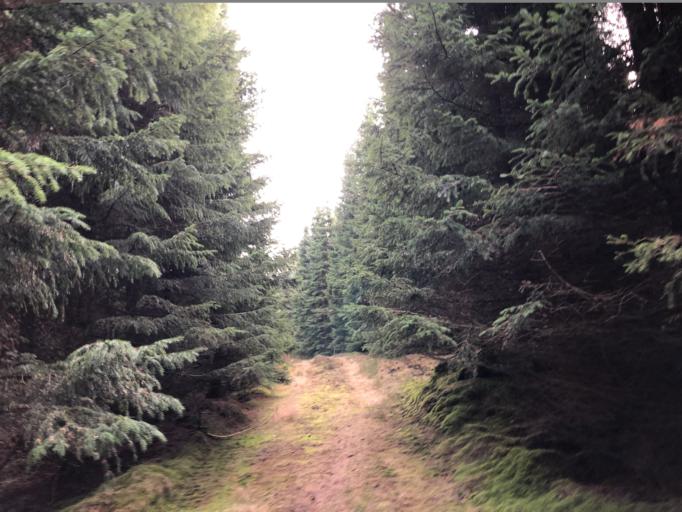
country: DK
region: Central Jutland
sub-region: Holstebro Kommune
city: Ulfborg
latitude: 56.2590
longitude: 8.3651
